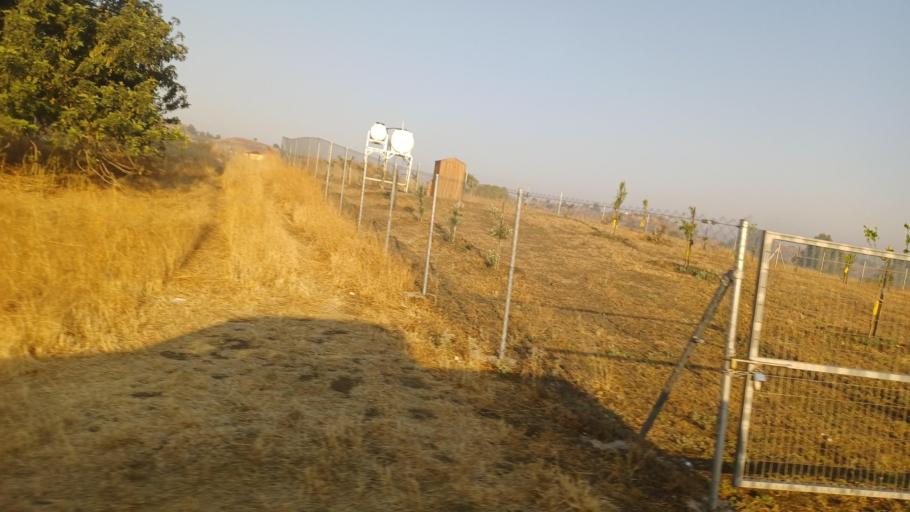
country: CY
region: Larnaka
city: Mosfiloti
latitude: 34.9703
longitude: 33.4316
